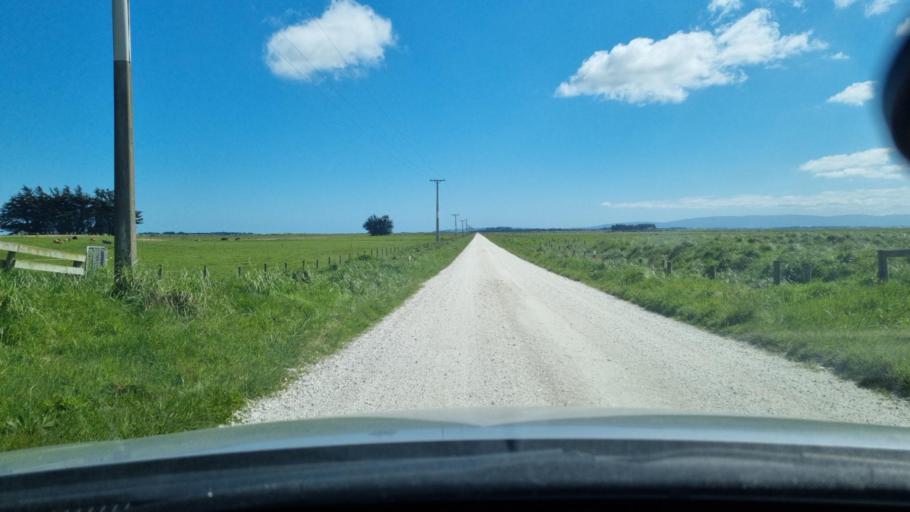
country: NZ
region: Southland
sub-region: Invercargill City
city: Invercargill
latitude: -46.3692
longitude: 168.2774
